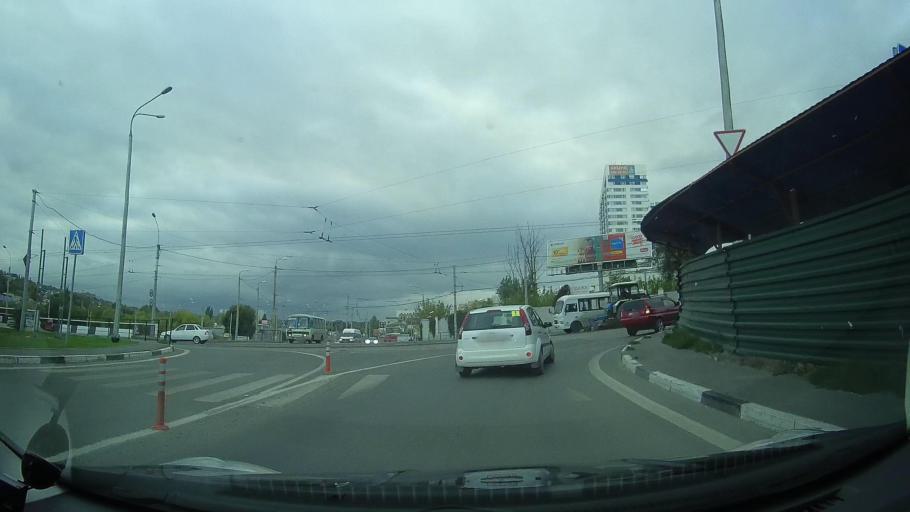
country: RU
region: Rostov
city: Rostov-na-Donu
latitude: 47.2222
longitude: 39.6925
